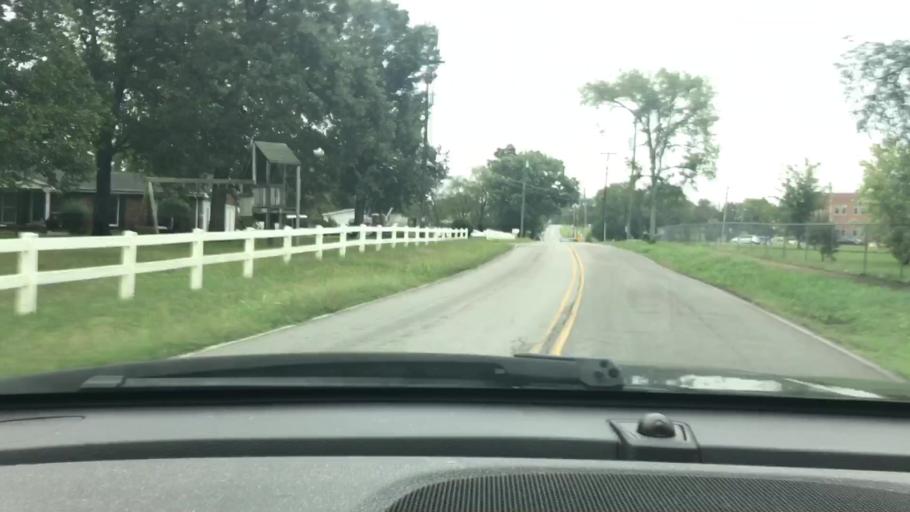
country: US
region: Tennessee
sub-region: Rutherford County
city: La Vergne
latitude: 36.0243
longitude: -86.5678
